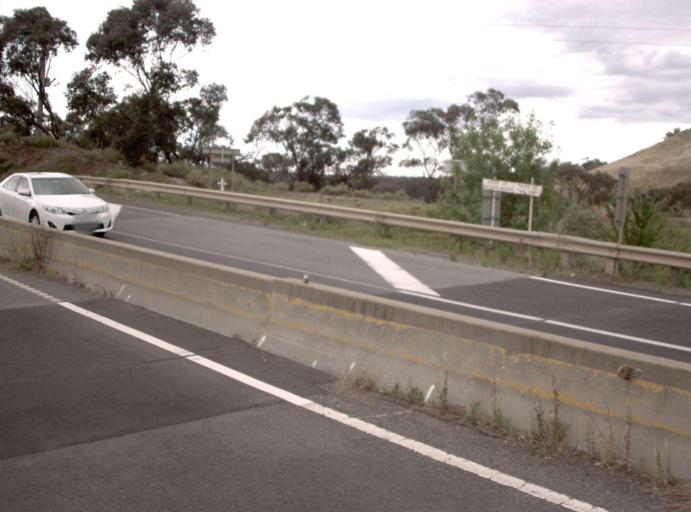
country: AU
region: Victoria
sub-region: Melton
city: Brookfield
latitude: -37.6856
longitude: 144.5147
